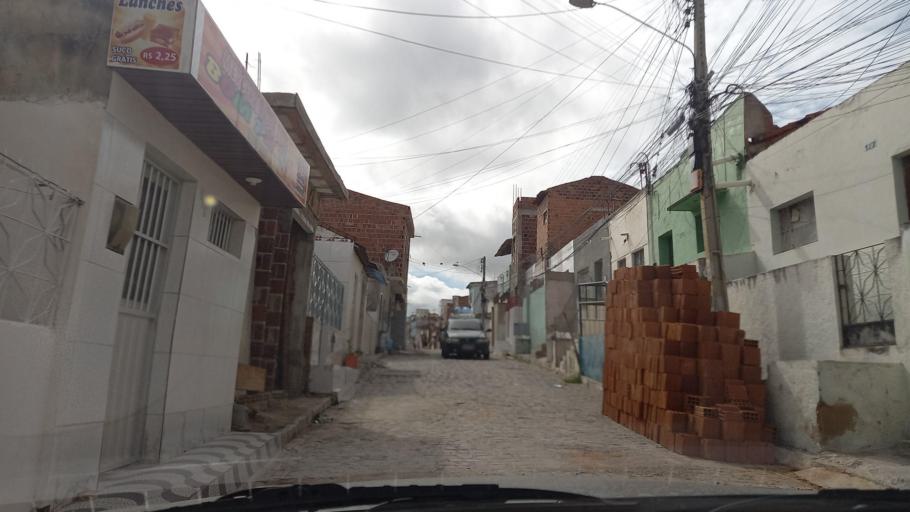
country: BR
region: Pernambuco
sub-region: Caruaru
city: Caruaru
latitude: -8.2825
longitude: -35.9784
